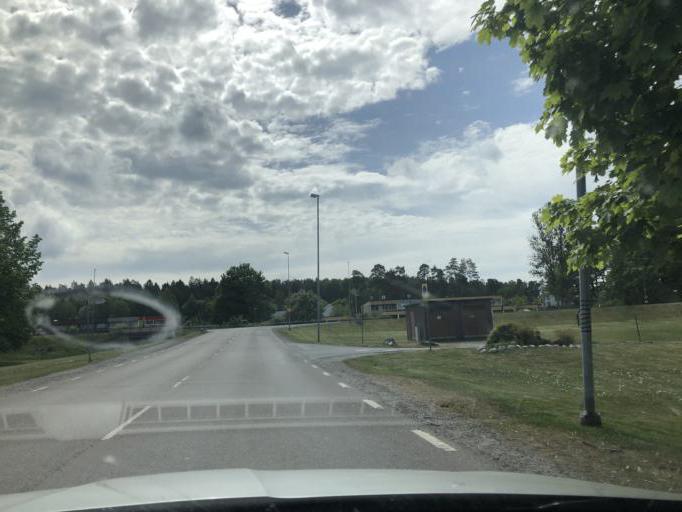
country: SE
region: Stockholm
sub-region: Botkyrka Kommun
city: Alby
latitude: 59.2344
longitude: 17.8515
